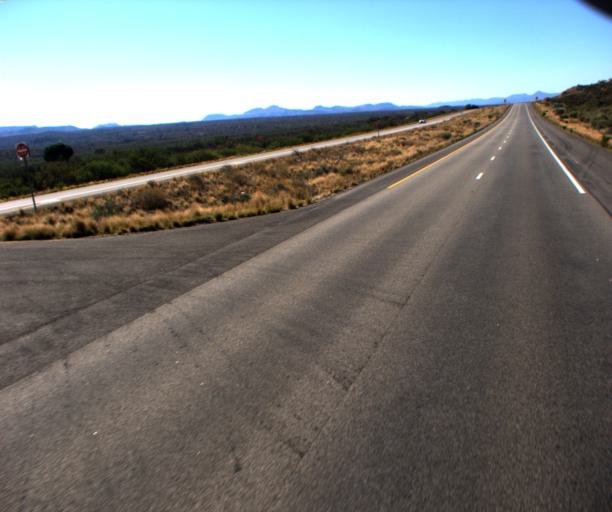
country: US
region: Arizona
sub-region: Yavapai County
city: Bagdad
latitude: 34.8317
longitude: -113.6312
